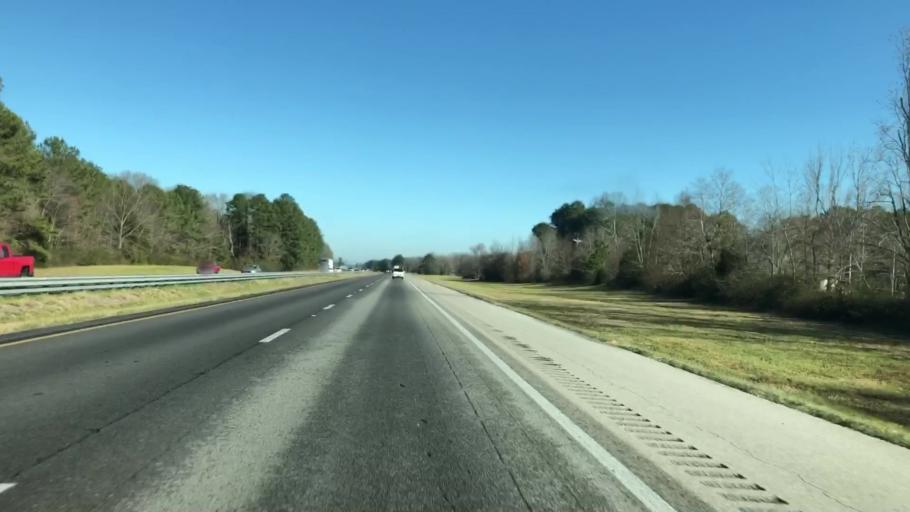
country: US
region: Alabama
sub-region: Limestone County
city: Athens
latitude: 34.8488
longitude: -86.9309
